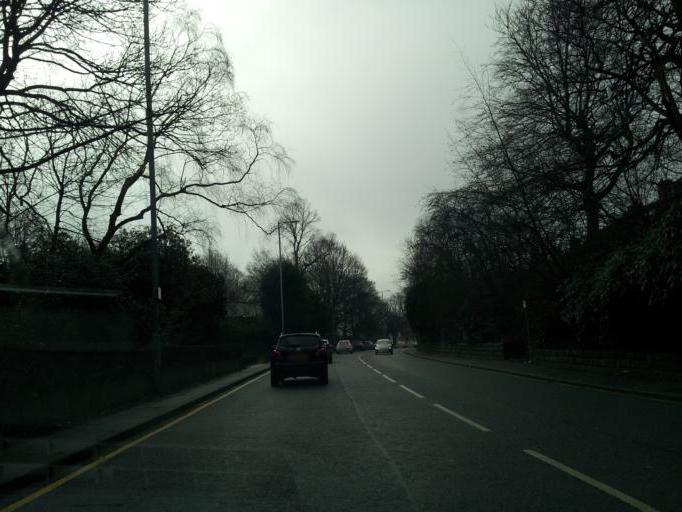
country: GB
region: England
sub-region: Manchester
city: Blackley
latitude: 53.5196
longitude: -2.2134
